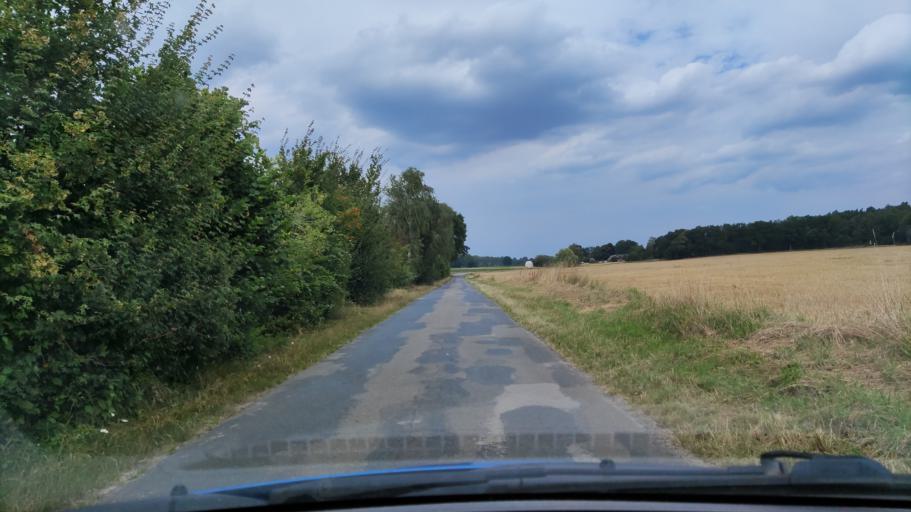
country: DE
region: Lower Saxony
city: Schnega
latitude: 52.9332
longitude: 10.8798
